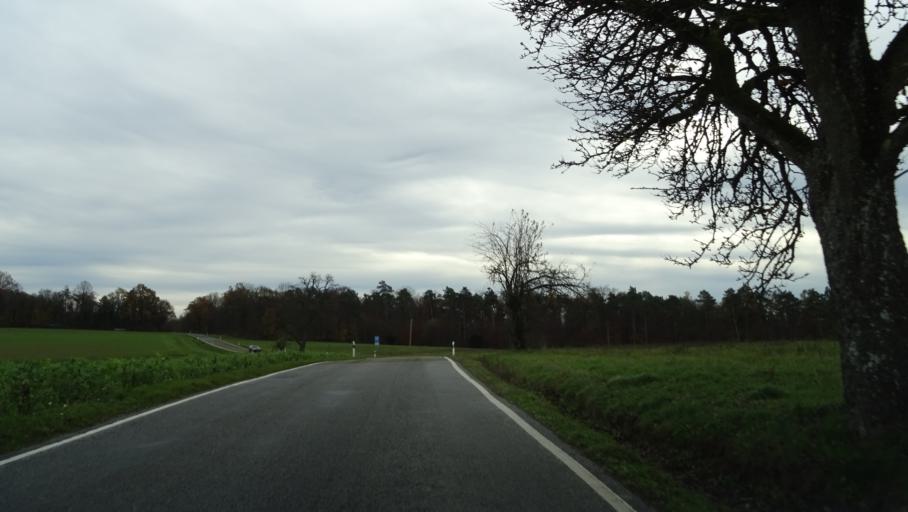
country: DE
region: Baden-Wuerttemberg
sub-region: Karlsruhe Region
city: Neckargerach
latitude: 49.3873
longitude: 9.1008
